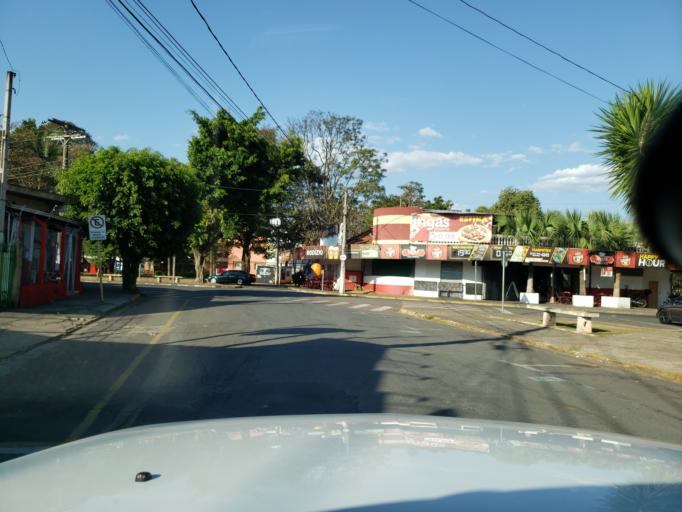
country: BR
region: Sao Paulo
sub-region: Moji-Guacu
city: Mogi-Gaucu
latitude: -22.3723
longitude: -46.9402
